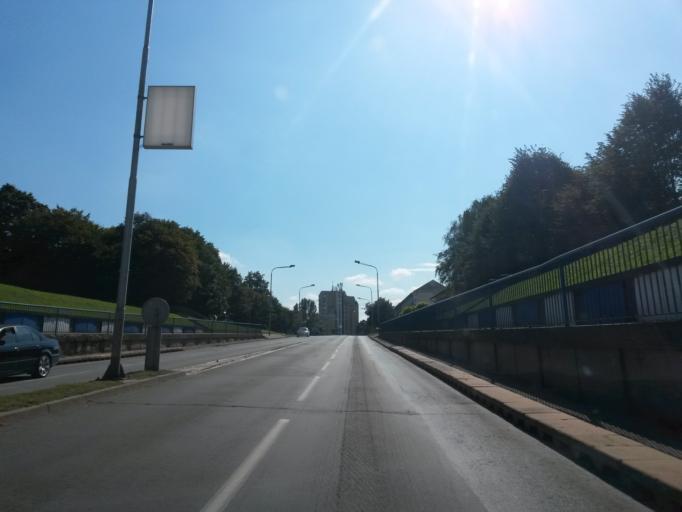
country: HR
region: Osjecko-Baranjska
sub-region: Grad Osijek
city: Osijek
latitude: 45.5529
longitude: 18.6946
